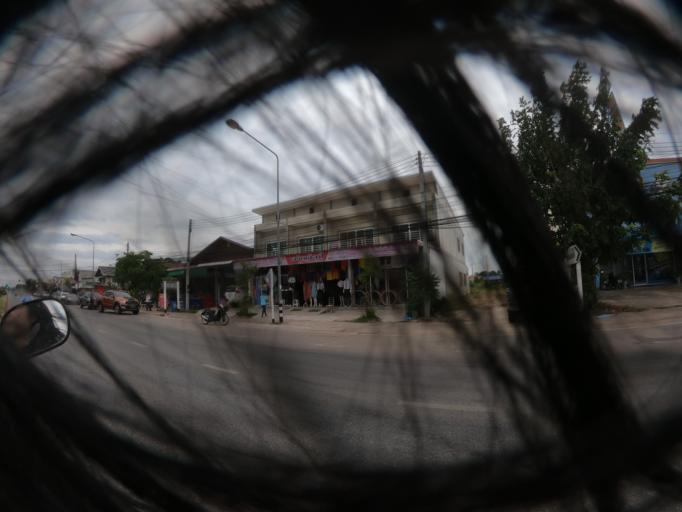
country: TH
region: Roi Et
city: Chiang Khwan
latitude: 16.1523
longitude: 103.8622
